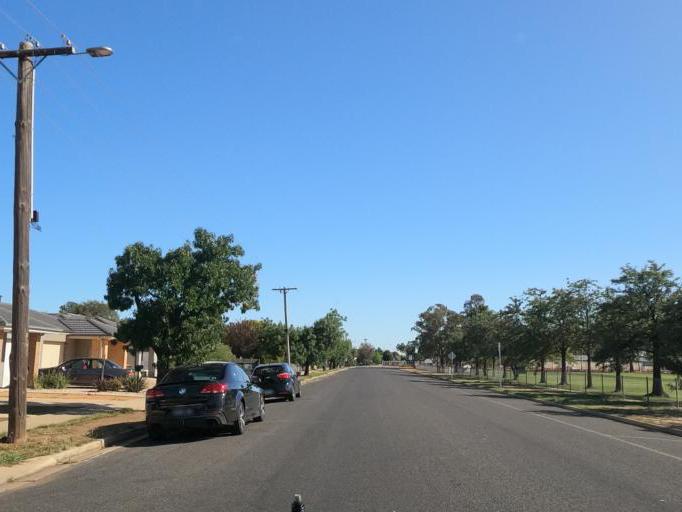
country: AU
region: Victoria
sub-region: Moira
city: Yarrawonga
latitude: -36.0206
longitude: 146.0054
